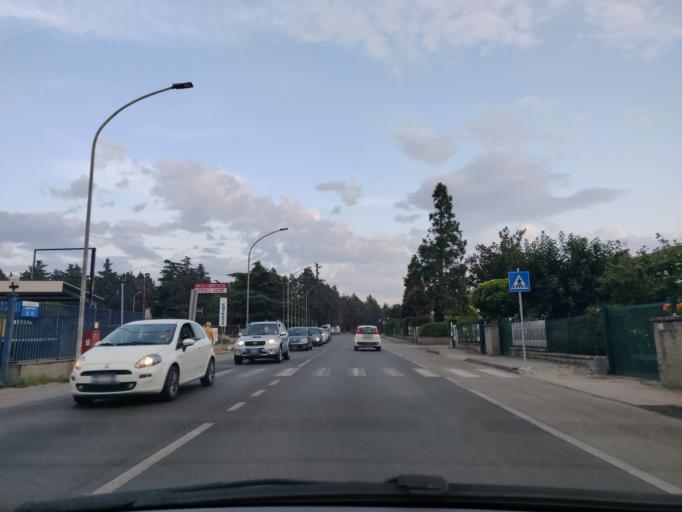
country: IT
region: Latium
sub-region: Provincia di Viterbo
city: Viterbo
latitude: 42.4365
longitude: 12.0964
